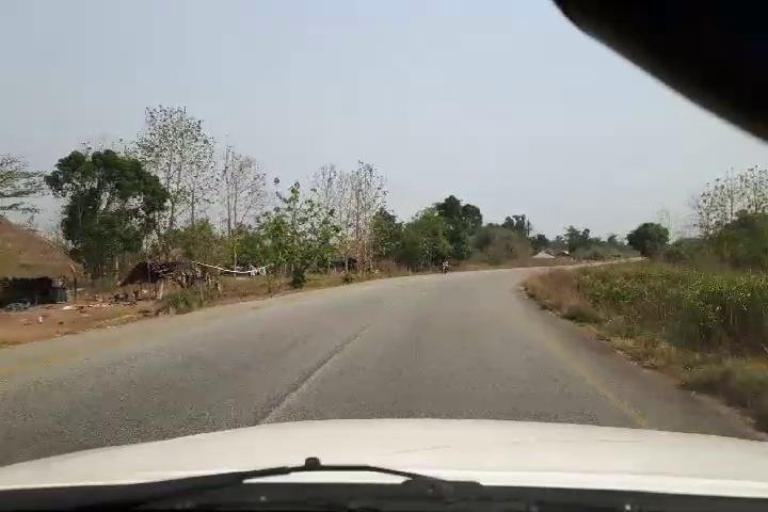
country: SL
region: Southern Province
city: Largo
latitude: 8.2976
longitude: -12.1995
